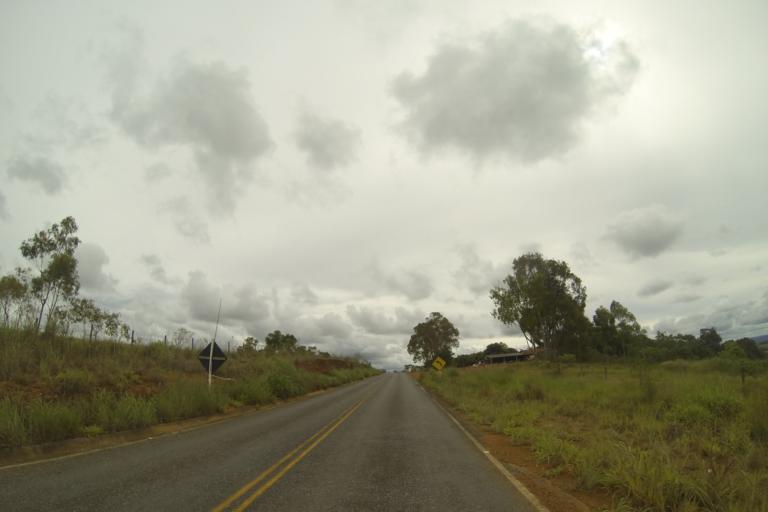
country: BR
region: Minas Gerais
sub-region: Ibia
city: Ibia
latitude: -19.6725
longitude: -46.4386
